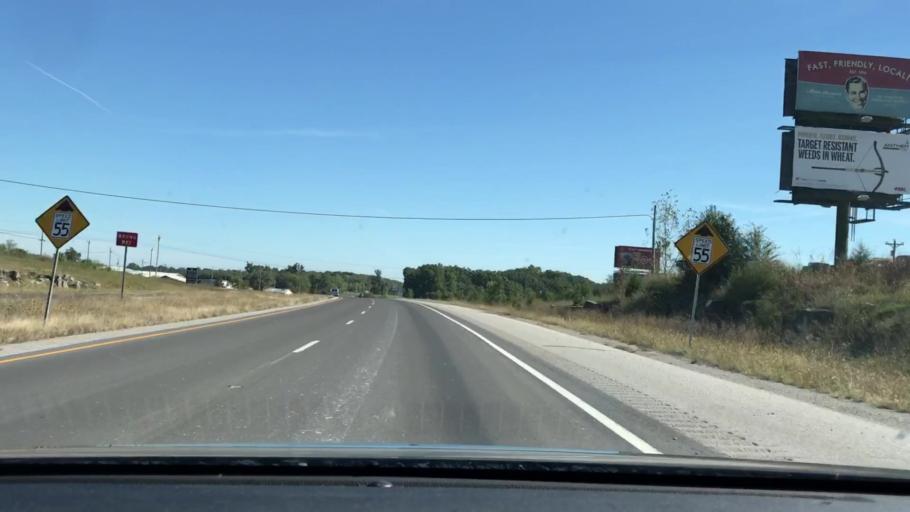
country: US
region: Kentucky
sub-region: Logan County
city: Russellville
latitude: 36.8369
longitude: -86.9277
